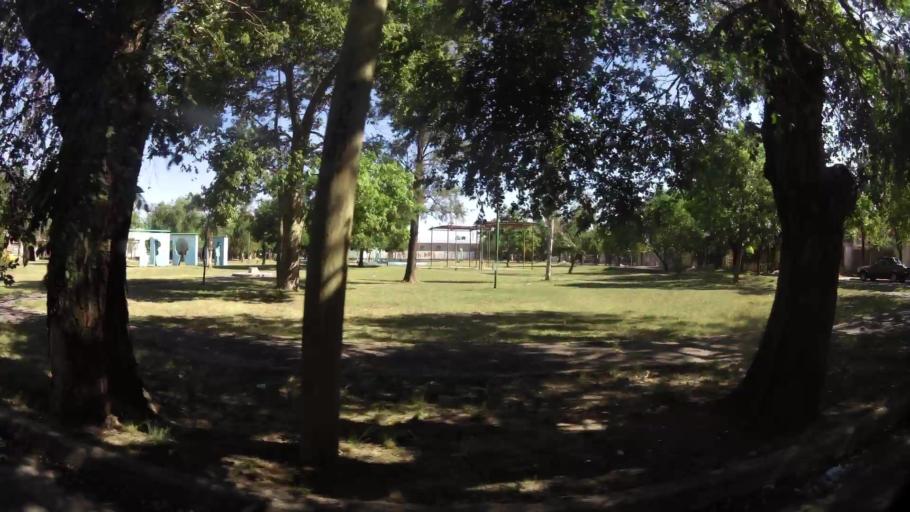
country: AR
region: Cordoba
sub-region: Departamento de Capital
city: Cordoba
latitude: -31.3651
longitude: -64.1727
